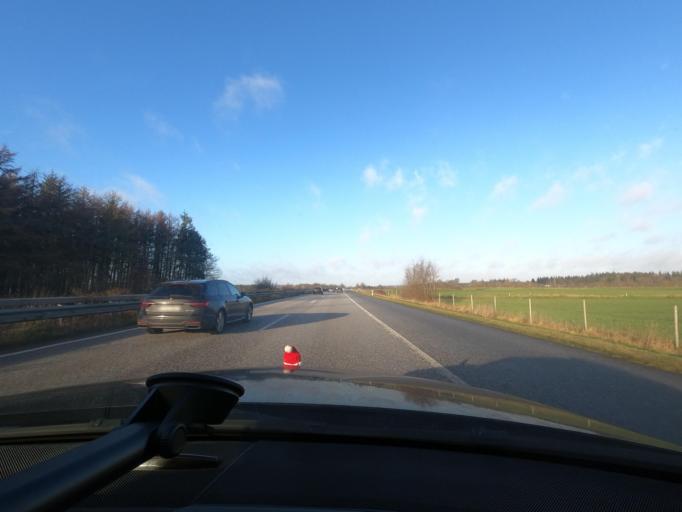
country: DE
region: Schleswig-Holstein
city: Bollingstedt
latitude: 54.6097
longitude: 9.4468
